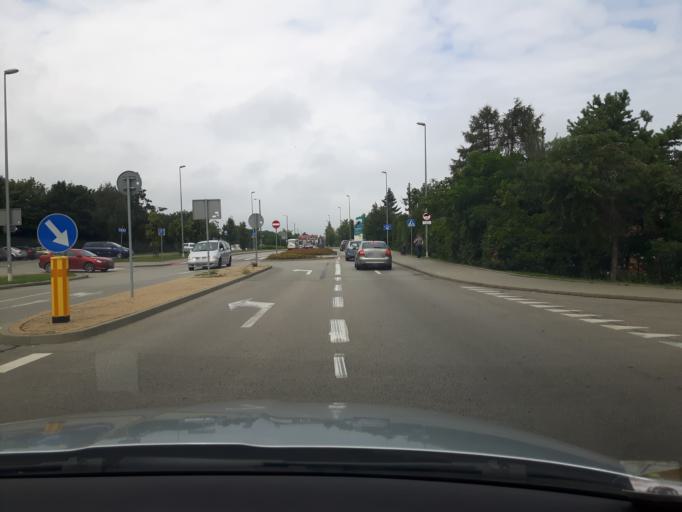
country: PL
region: Pomeranian Voivodeship
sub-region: Sopot
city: Sopot
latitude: 54.4257
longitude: 18.5766
